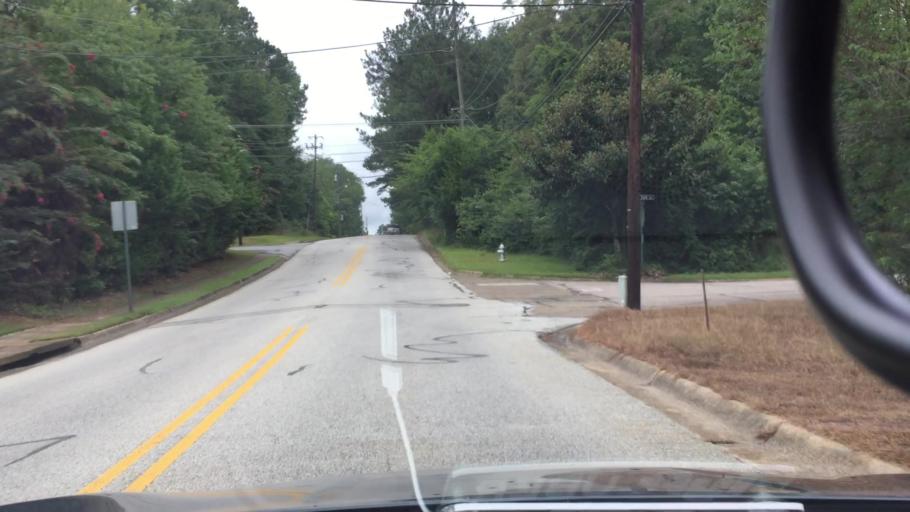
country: US
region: Alabama
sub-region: Lee County
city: Auburn
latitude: 32.6141
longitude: -85.4855
